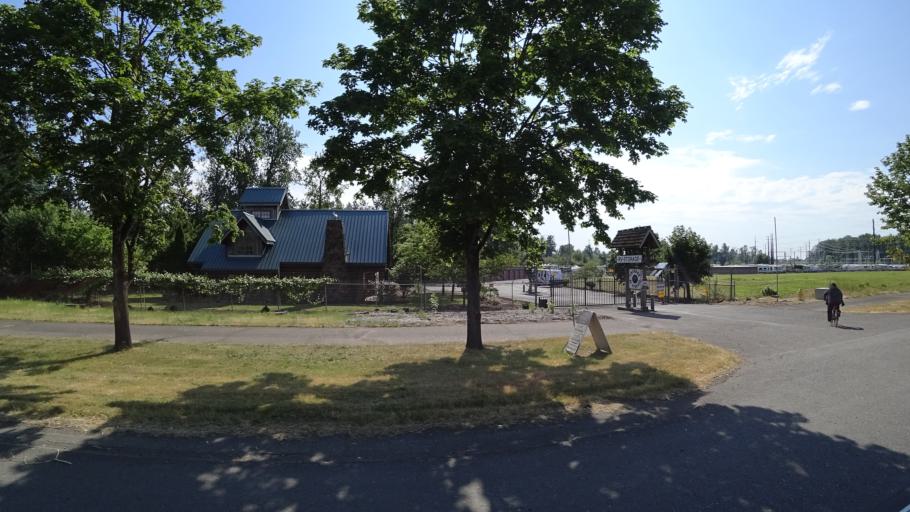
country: US
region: Oregon
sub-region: Multnomah County
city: Fairview
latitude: 45.5535
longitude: -122.4240
